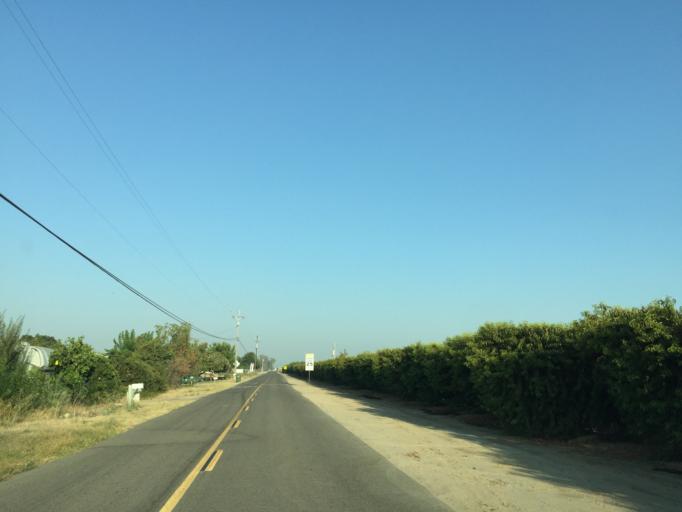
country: US
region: California
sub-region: Tulare County
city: London
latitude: 36.4591
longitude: -119.4770
